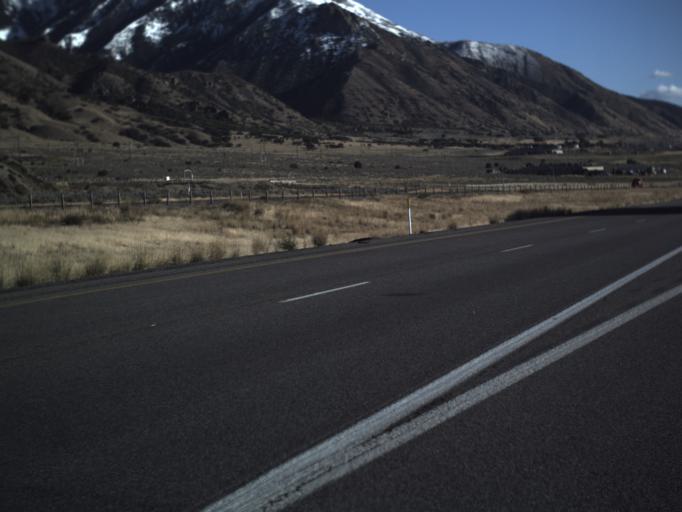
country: US
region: Utah
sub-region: Juab County
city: Mona
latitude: 39.8258
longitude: -111.8340
